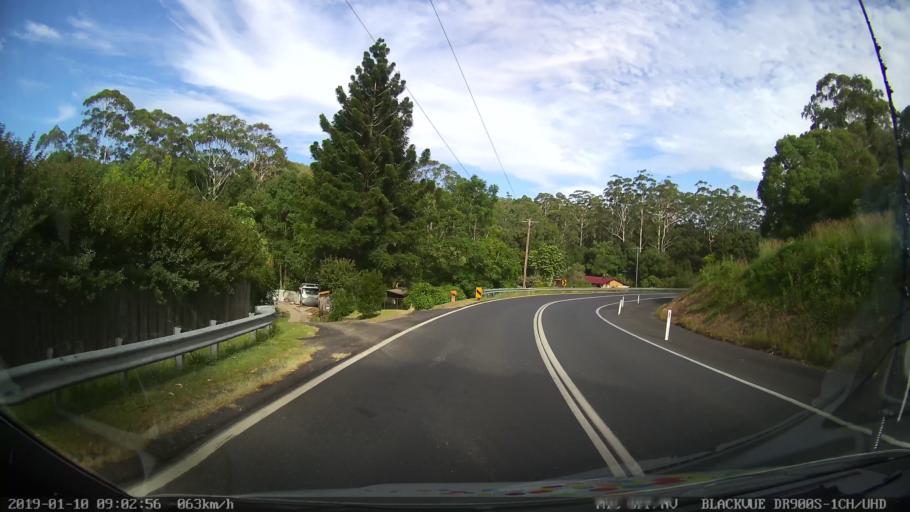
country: AU
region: New South Wales
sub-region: Coffs Harbour
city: Coffs Harbour
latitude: -30.2685
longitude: 153.0495
